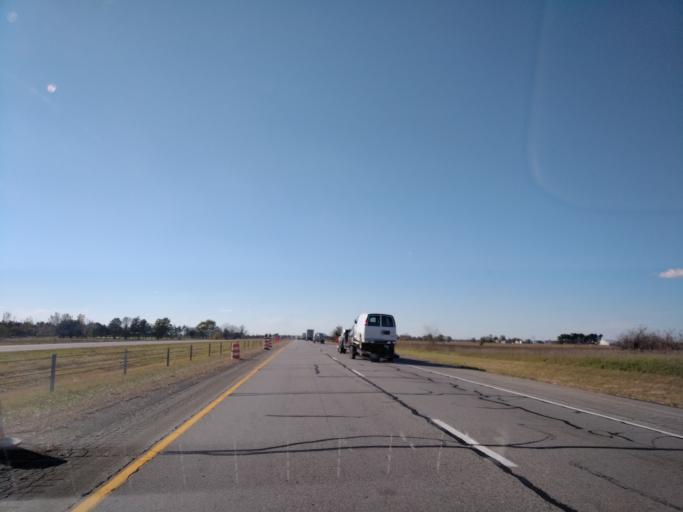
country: US
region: Indiana
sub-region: Henry County
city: Knightstown
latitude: 39.8260
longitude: -85.6314
